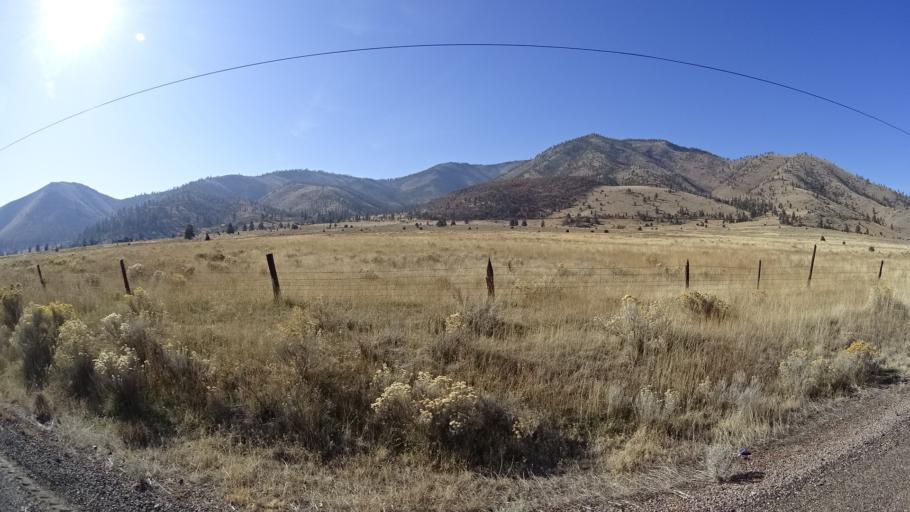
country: US
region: California
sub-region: Siskiyou County
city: Weed
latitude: 41.4781
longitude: -122.4891
